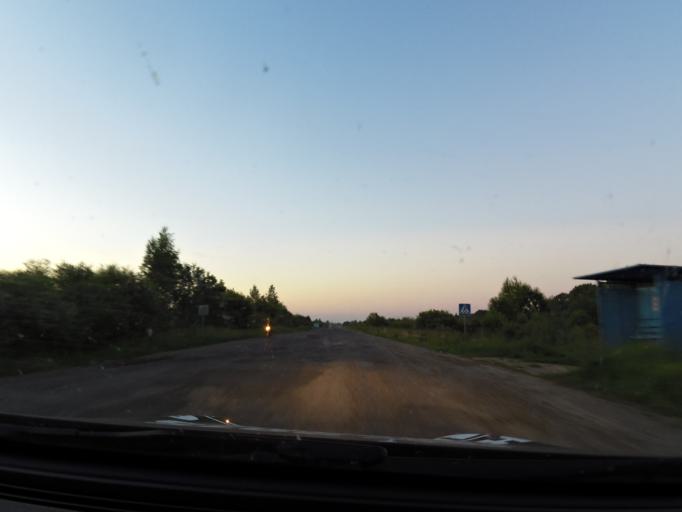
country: RU
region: Kostroma
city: Buy
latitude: 58.4642
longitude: 41.4097
